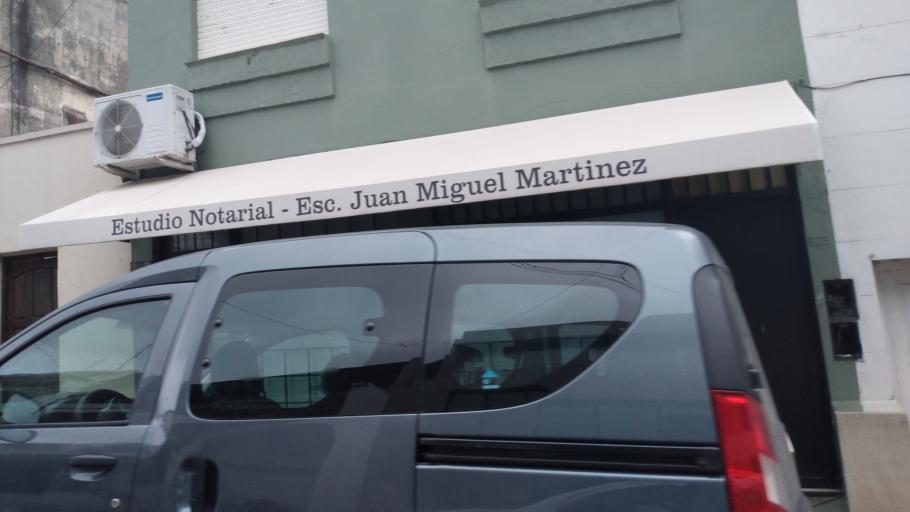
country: AR
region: Corrientes
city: Corrientes
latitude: -27.4663
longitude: -58.8388
